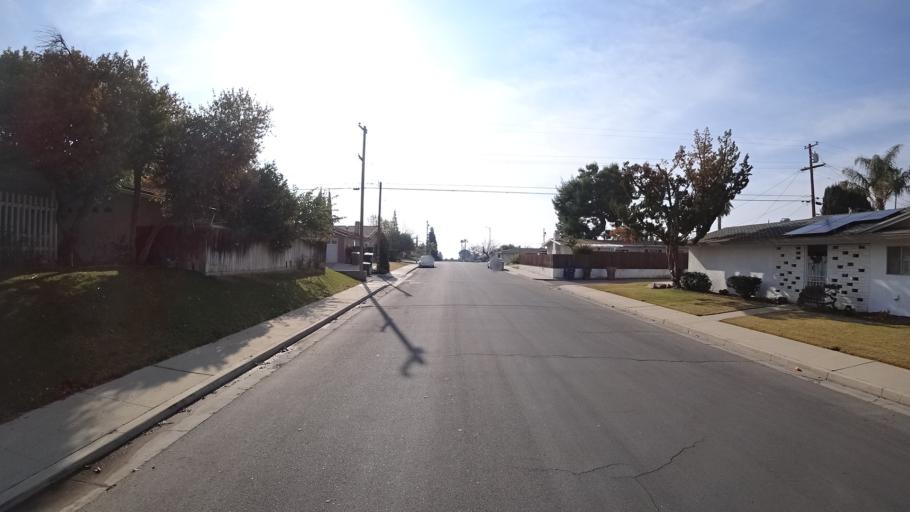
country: US
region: California
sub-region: Kern County
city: Oildale
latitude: 35.4081
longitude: -118.9545
